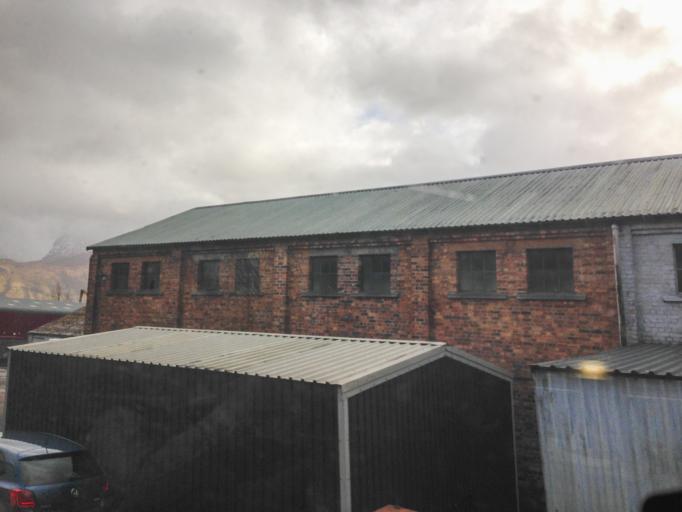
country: GB
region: Scotland
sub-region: Highland
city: Fort William
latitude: 56.8430
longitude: -5.1394
